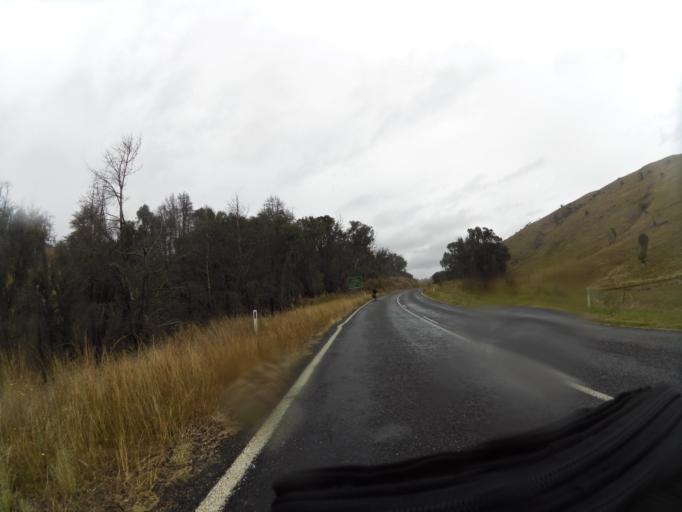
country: AU
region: New South Wales
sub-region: Greater Hume Shire
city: Holbrook
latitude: -36.2238
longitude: 147.7274
